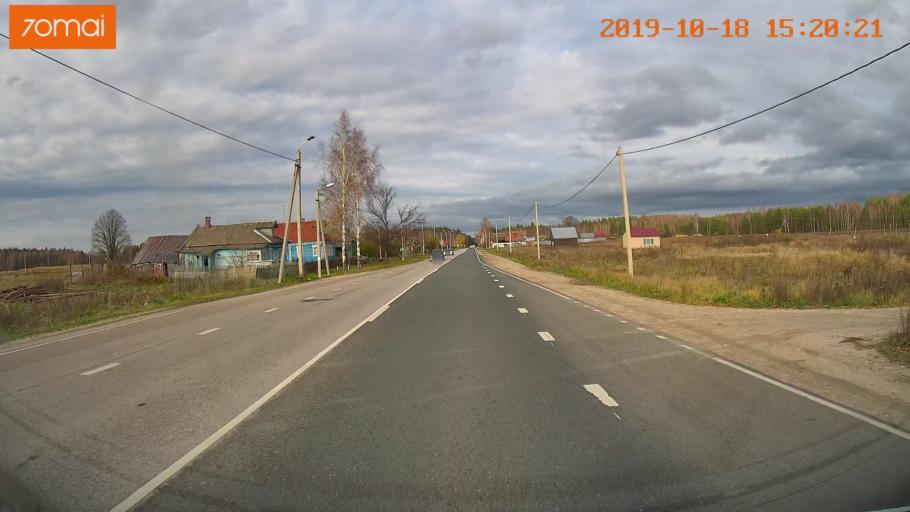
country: RU
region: Vladimir
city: Anopino
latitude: 55.6859
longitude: 40.7442
